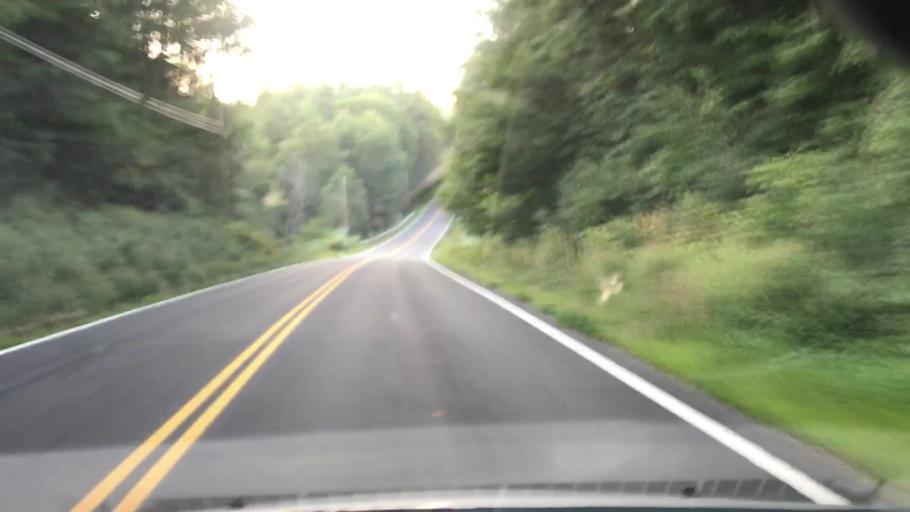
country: US
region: New Hampshire
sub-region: Grafton County
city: Woodsville
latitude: 44.1894
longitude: -72.0535
